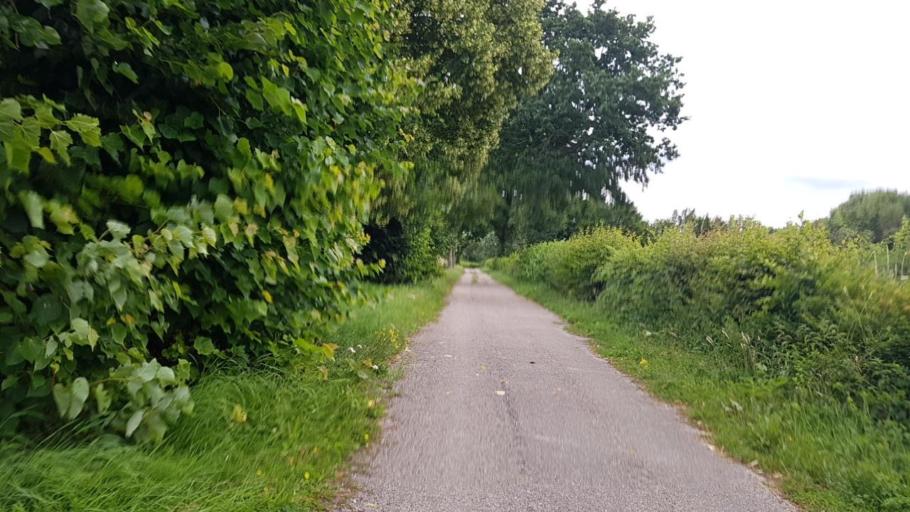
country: FR
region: Picardie
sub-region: Departement de l'Aisne
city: Origny-en-Thierache
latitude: 49.9257
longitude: 3.9691
